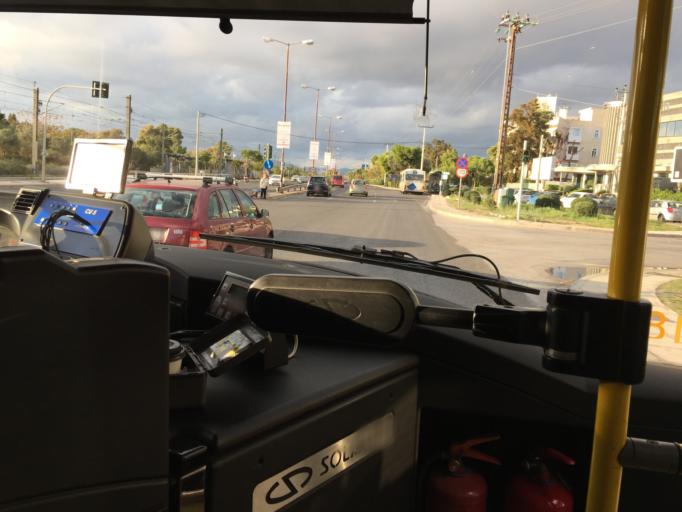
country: GR
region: Attica
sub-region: Nomarchia Athinas
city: Elliniko
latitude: 37.8802
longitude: 23.7304
